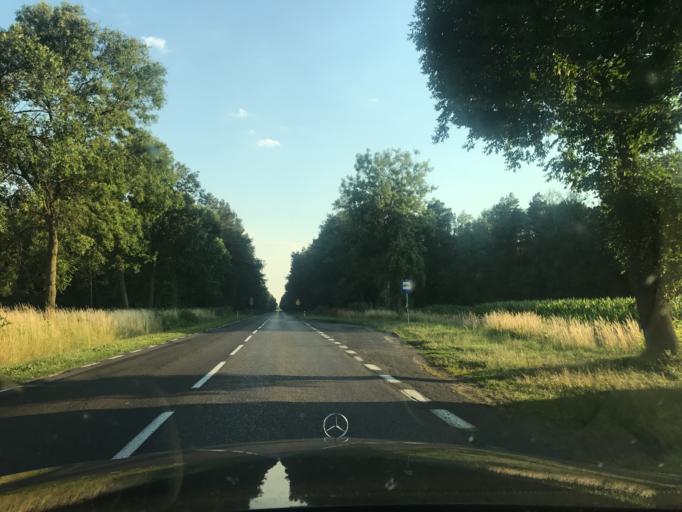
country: PL
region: Lublin Voivodeship
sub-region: Powiat parczewski
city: Debowa Kloda
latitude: 51.6697
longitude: 23.0144
